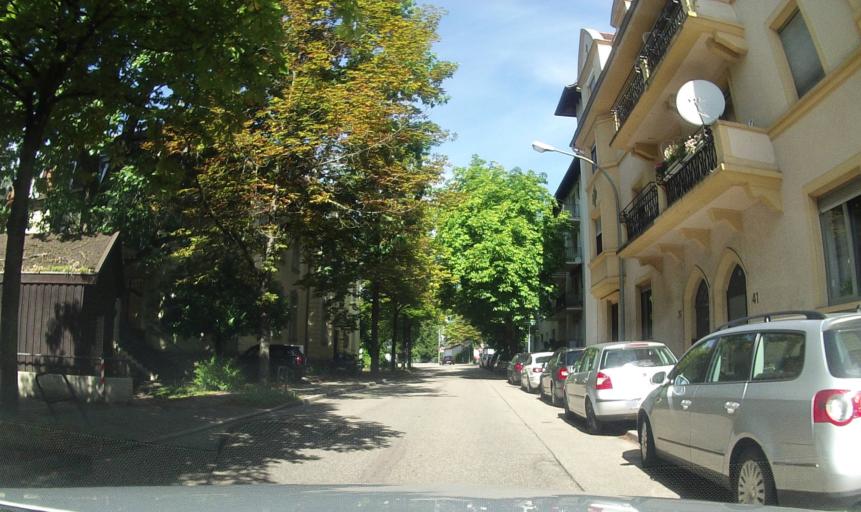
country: DE
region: Baden-Wuerttemberg
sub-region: Karlsruhe Region
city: Baden-Baden
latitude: 48.7502
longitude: 8.2539
